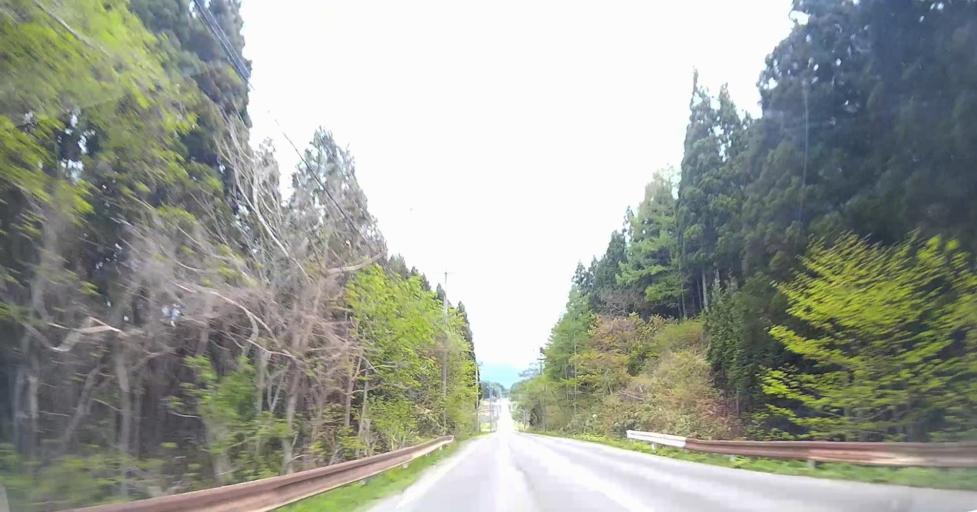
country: JP
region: Aomori
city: Goshogawara
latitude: 41.1783
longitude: 140.4737
